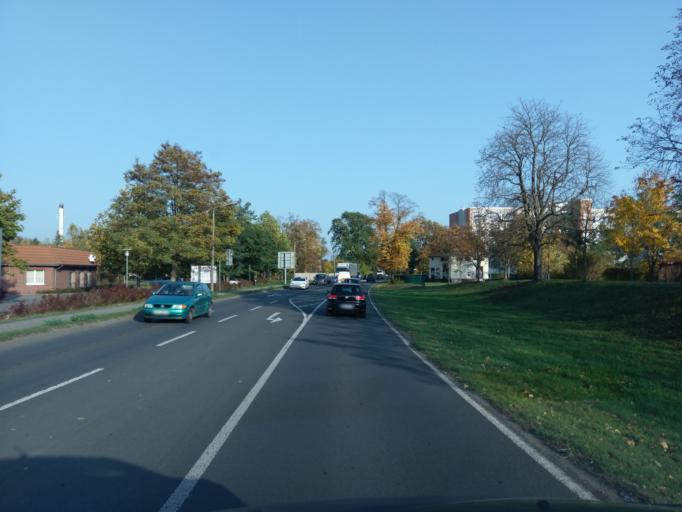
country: DE
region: Brandenburg
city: Herzberg
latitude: 51.6951
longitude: 13.2372
